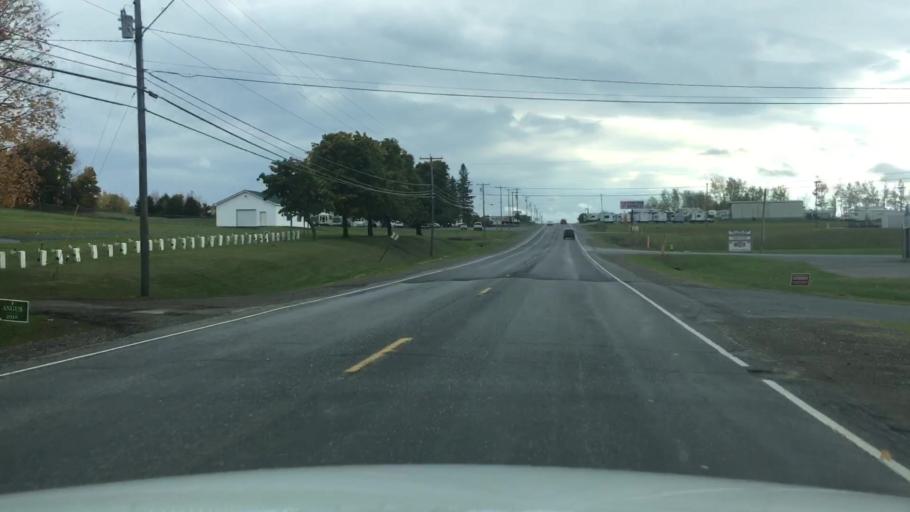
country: US
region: Maine
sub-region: Aroostook County
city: Presque Isle
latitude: 46.6627
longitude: -68.0091
